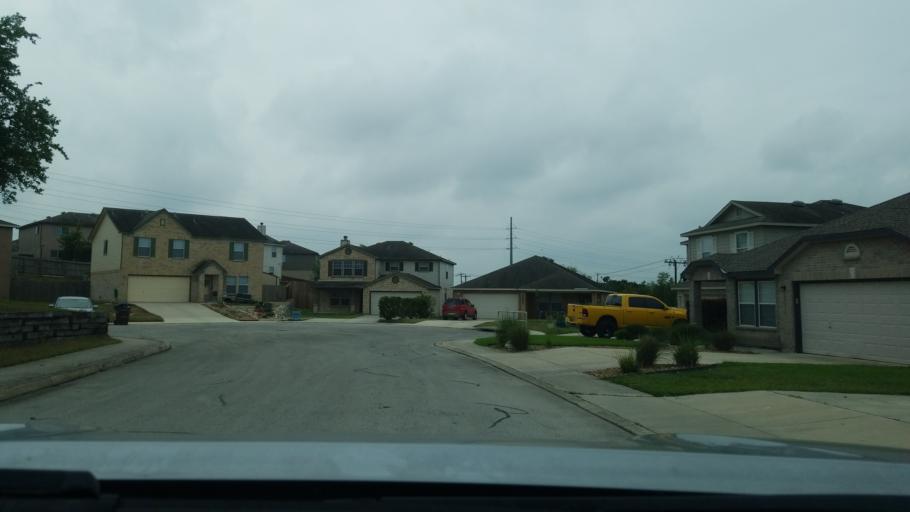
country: US
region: Texas
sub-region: Bexar County
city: Timberwood Park
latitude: 29.6813
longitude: -98.4680
